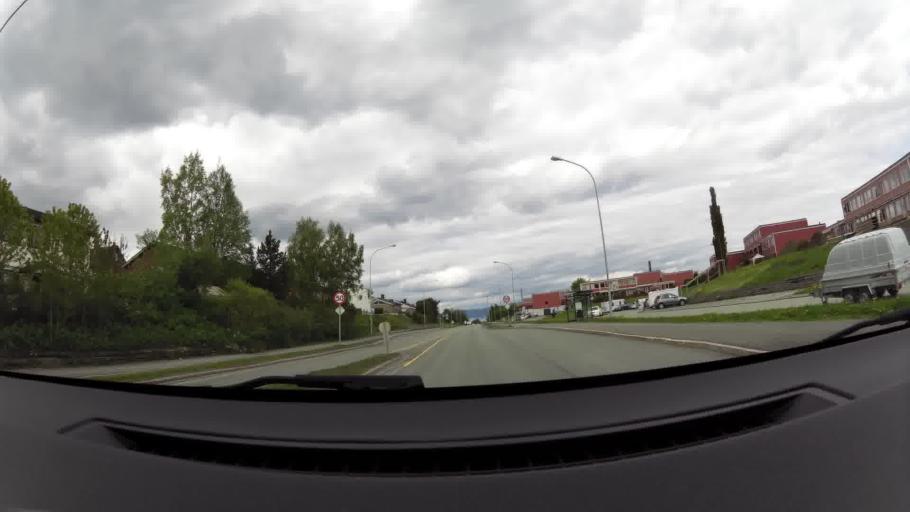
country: NO
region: Sor-Trondelag
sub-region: Trondheim
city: Trondheim
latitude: 63.3915
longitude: 10.4268
